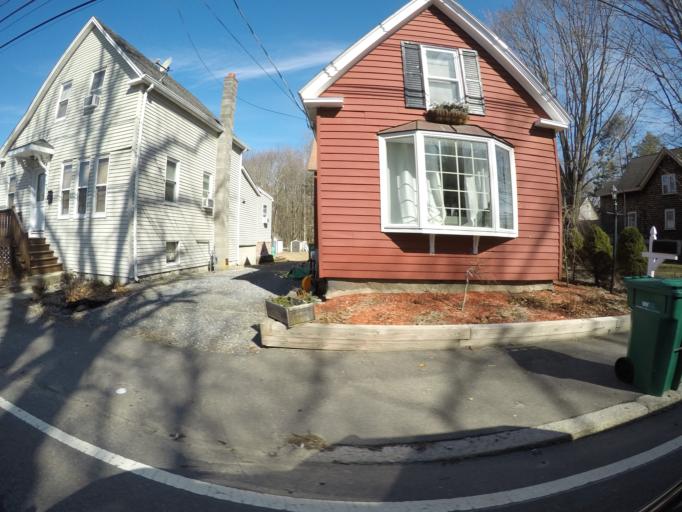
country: US
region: Massachusetts
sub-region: Bristol County
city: Easton
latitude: 42.0720
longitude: -71.1084
